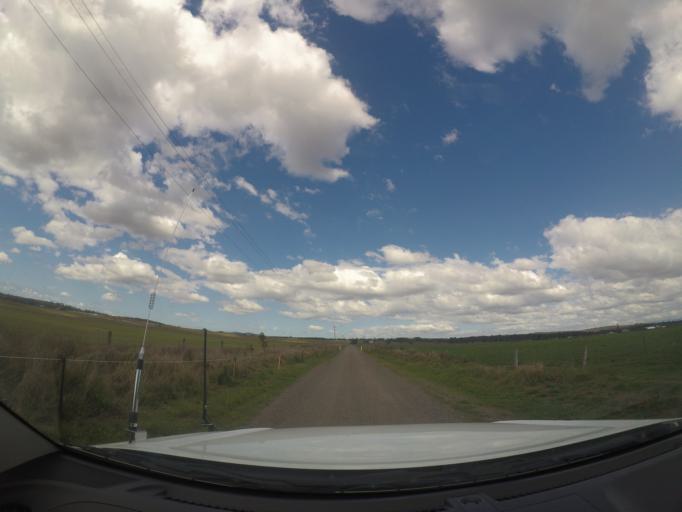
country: AU
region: Queensland
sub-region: Logan
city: Cedar Vale
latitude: -27.8522
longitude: 152.9560
